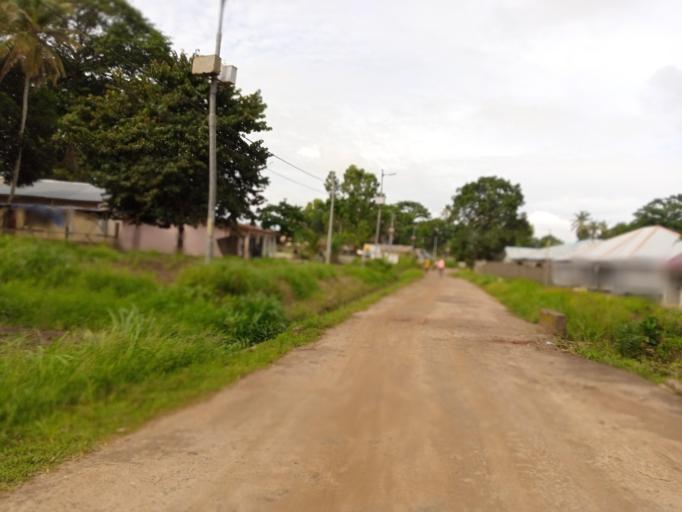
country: SL
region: Northern Province
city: Masoyila
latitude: 8.6048
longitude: -13.1984
